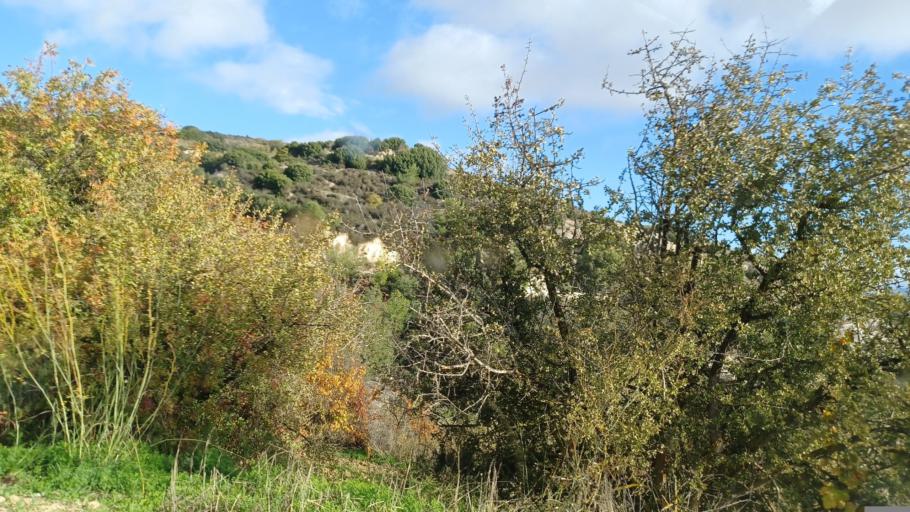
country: CY
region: Pafos
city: Mesogi
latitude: 34.8603
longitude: 32.5072
